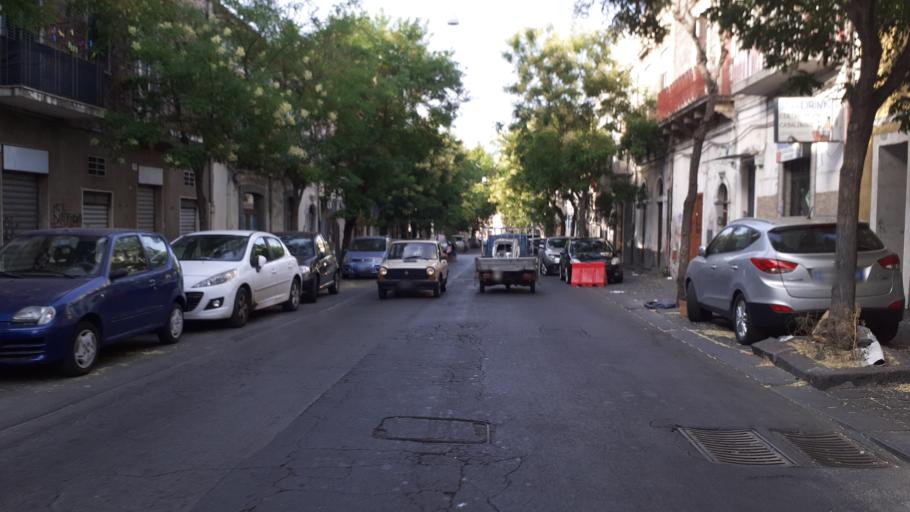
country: IT
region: Sicily
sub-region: Catania
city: Catania
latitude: 37.5062
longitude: 15.0787
